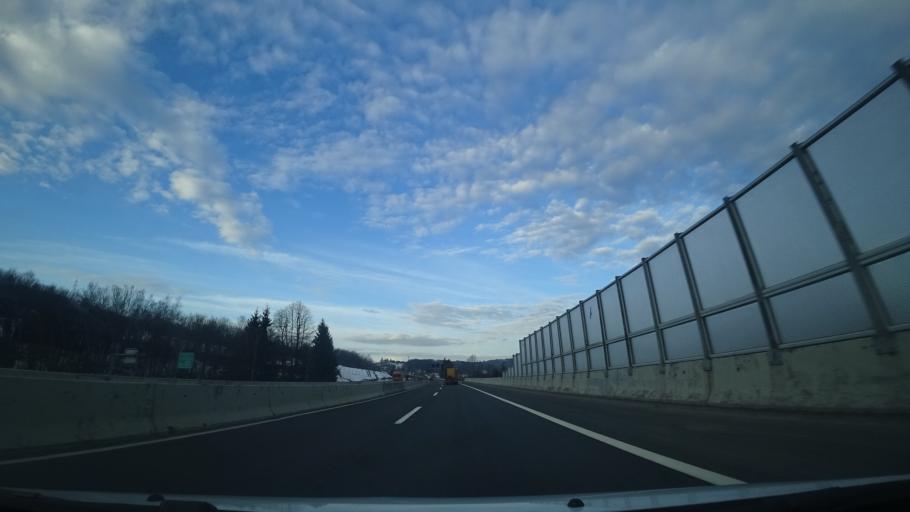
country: HR
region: Karlovacka
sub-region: Grad Karlovac
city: Karlovac
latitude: 45.5148
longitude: 15.4755
